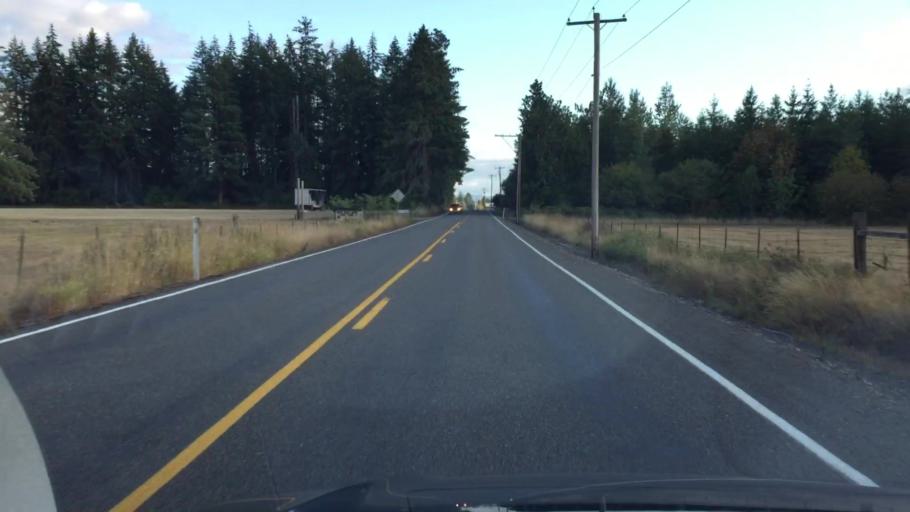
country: US
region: Washington
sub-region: Lewis County
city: Napavine
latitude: 46.5304
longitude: -122.7405
